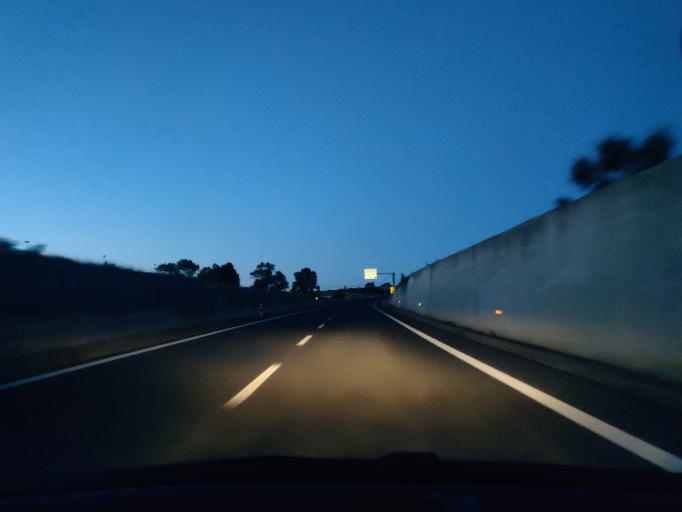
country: IT
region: Latium
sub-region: Citta metropolitana di Roma Capitale
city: Aurelia
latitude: 42.1245
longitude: 11.7912
